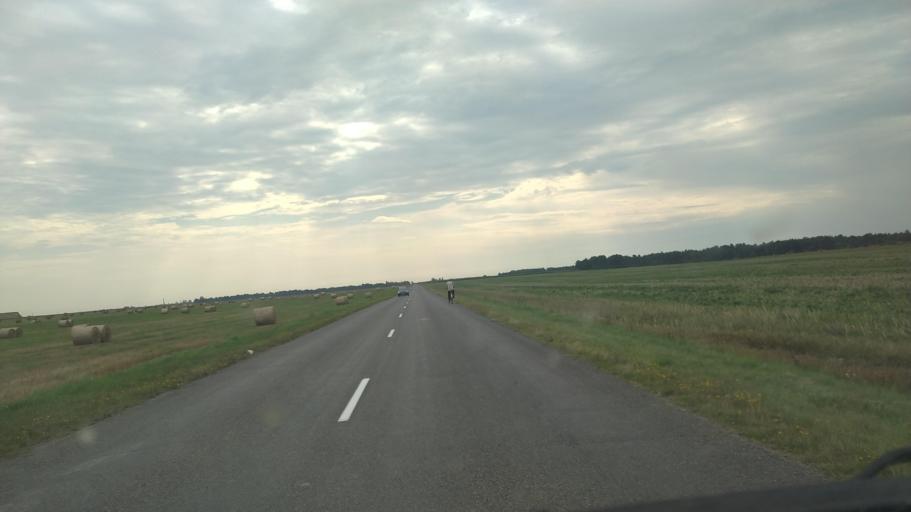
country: BY
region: Brest
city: Byaroza
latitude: 52.5751
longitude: 24.8749
